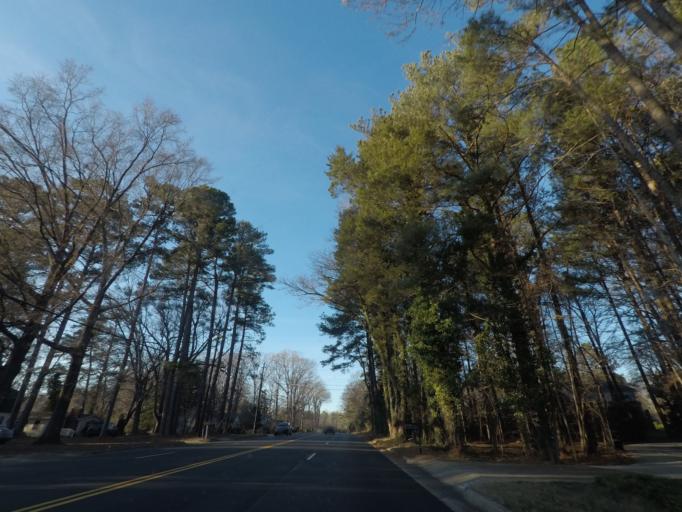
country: US
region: North Carolina
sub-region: Durham County
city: Durham
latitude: 36.0351
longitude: -78.9537
